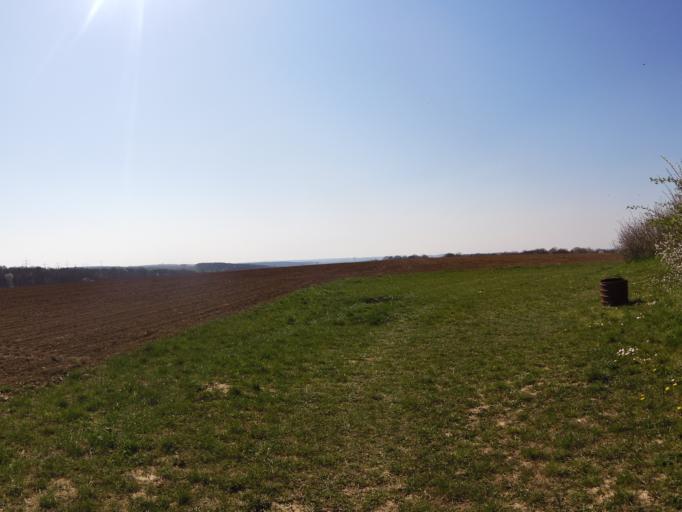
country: DE
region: Bavaria
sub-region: Regierungsbezirk Unterfranken
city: Rottendorf
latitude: 49.8159
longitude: 10.0762
